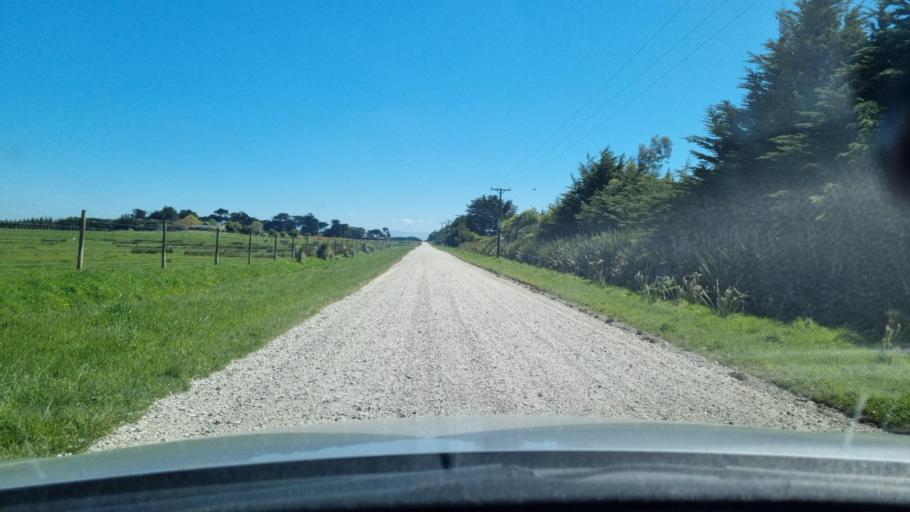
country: NZ
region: Southland
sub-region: Invercargill City
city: Invercargill
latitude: -46.4214
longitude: 168.2749
